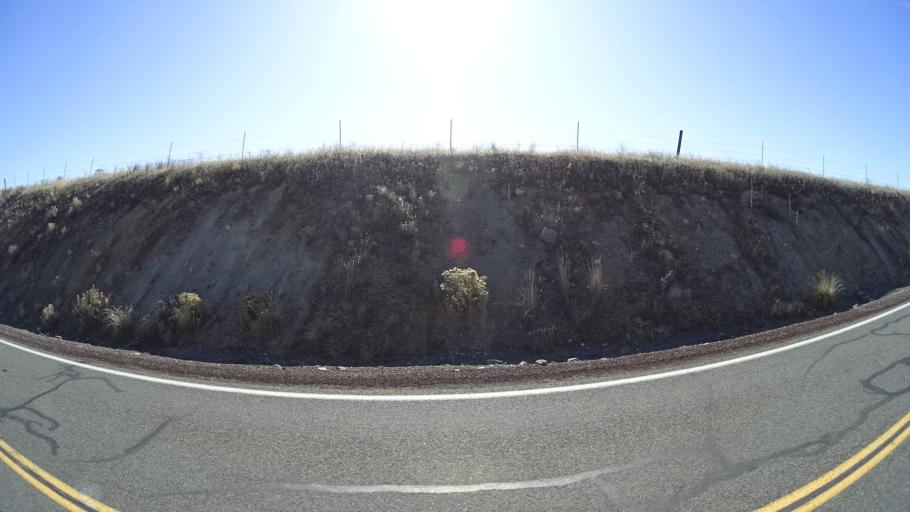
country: US
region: California
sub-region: Siskiyou County
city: Yreka
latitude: 41.7456
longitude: -122.5808
